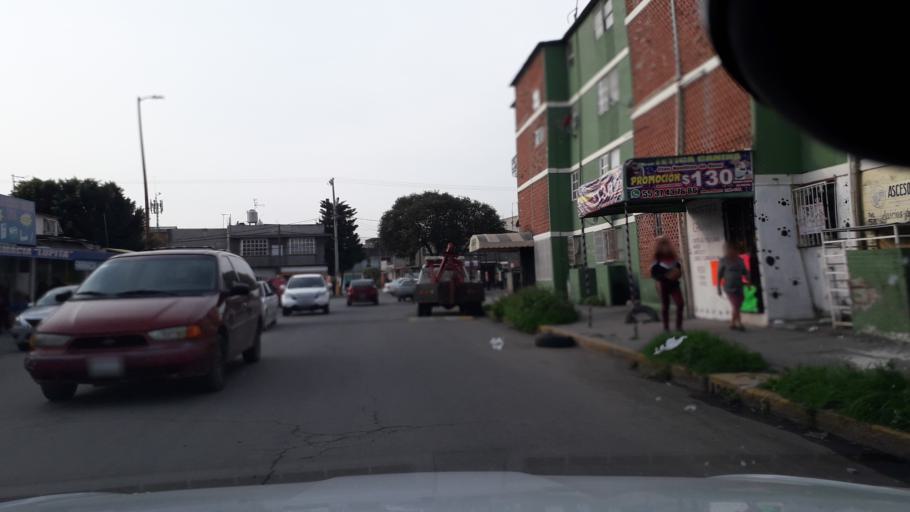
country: MX
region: Mexico
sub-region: Jaltenco
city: Alborada Jaltenco
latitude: 19.6597
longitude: -99.0683
